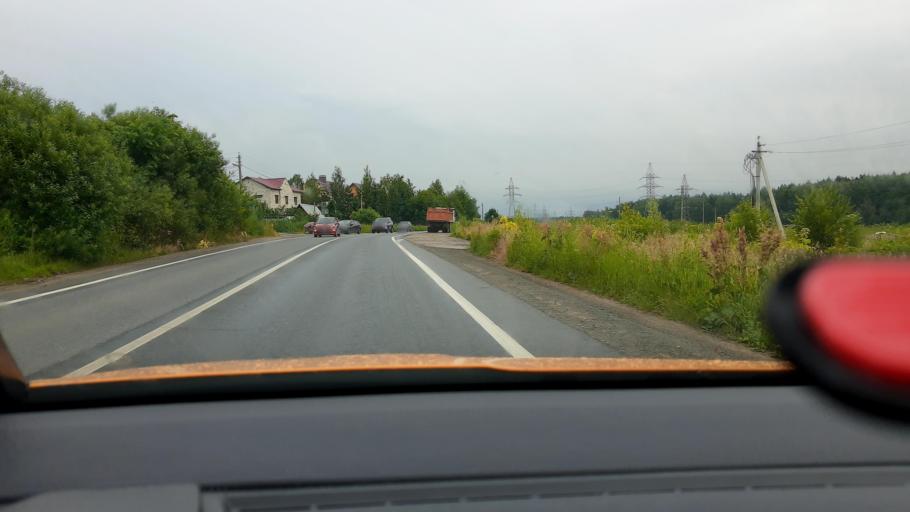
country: RU
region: Moskovskaya
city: Pirogovskiy
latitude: 55.9977
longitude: 37.7131
